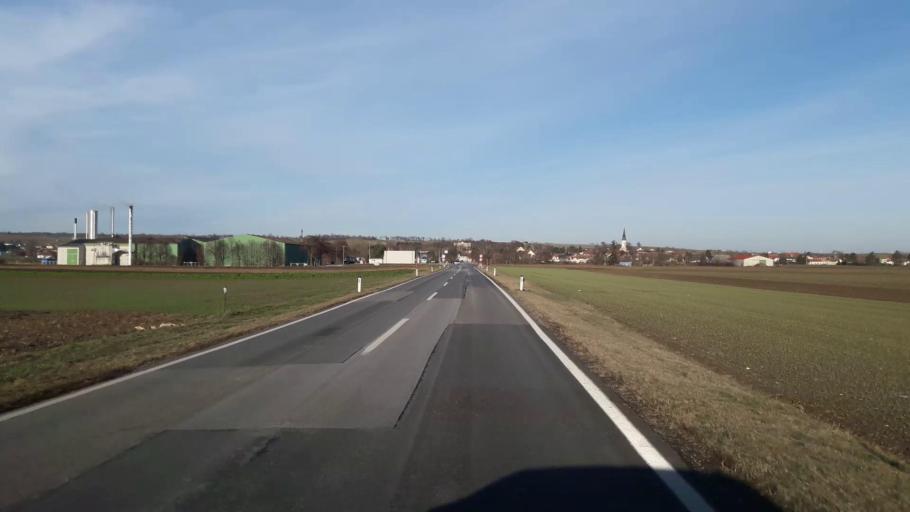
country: AT
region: Lower Austria
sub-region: Politischer Bezirk Mistelbach
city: Bockfliess
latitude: 48.3516
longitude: 16.5991
